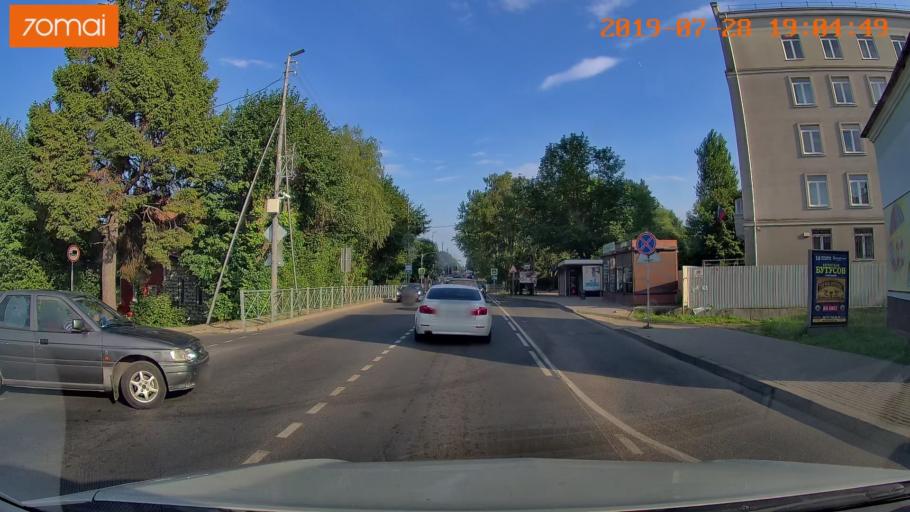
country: RU
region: Kaliningrad
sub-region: Gorod Svetlogorsk
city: Svetlogorsk
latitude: 54.9333
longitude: 20.1622
